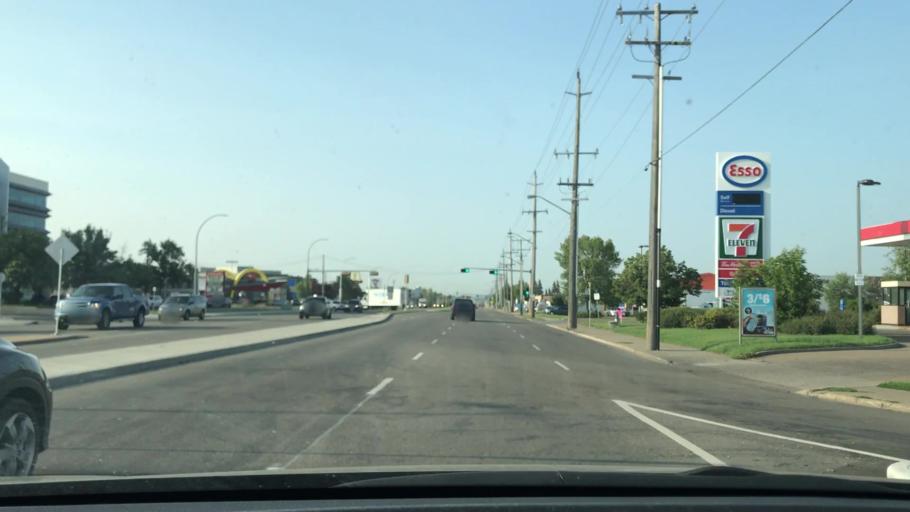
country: CA
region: Alberta
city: Edmonton
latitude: 53.5410
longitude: -113.4187
